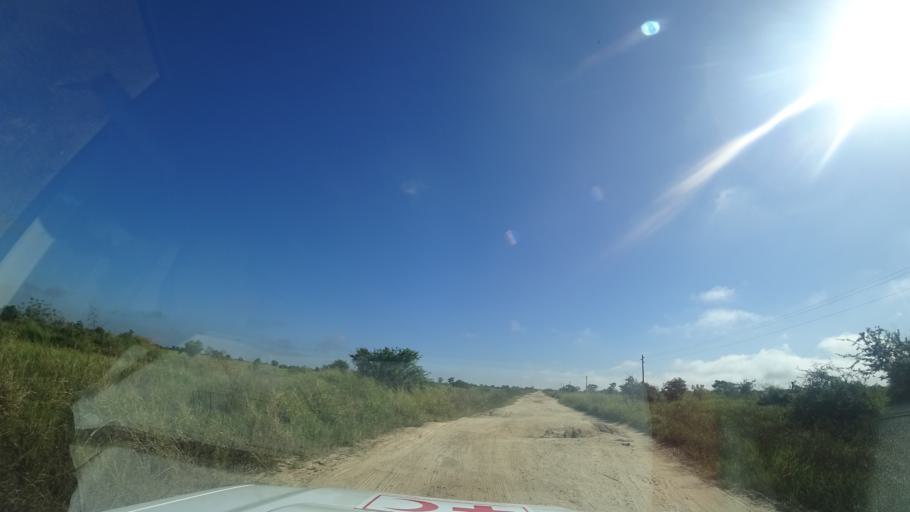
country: MZ
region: Sofala
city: Dondo
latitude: -19.4408
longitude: 34.5617
